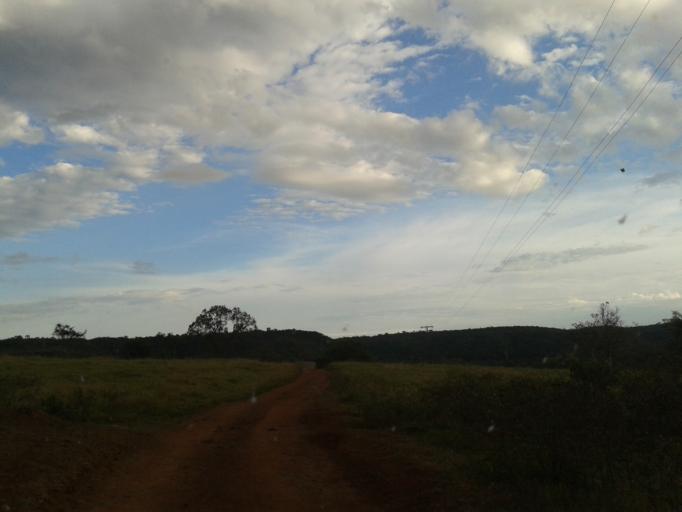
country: BR
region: Minas Gerais
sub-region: Campina Verde
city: Campina Verde
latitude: -19.3480
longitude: -49.6673
